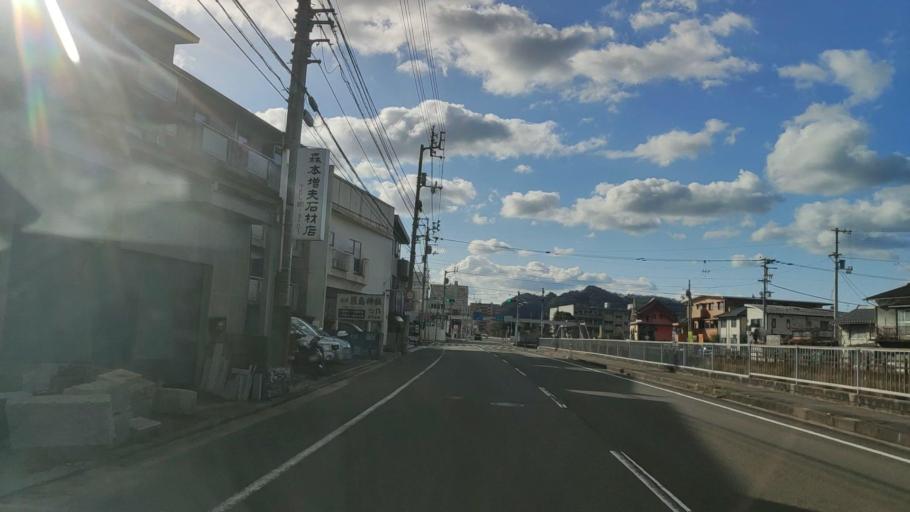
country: JP
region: Ehime
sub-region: Shikoku-chuo Shi
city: Matsuyama
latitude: 33.8594
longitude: 132.7194
